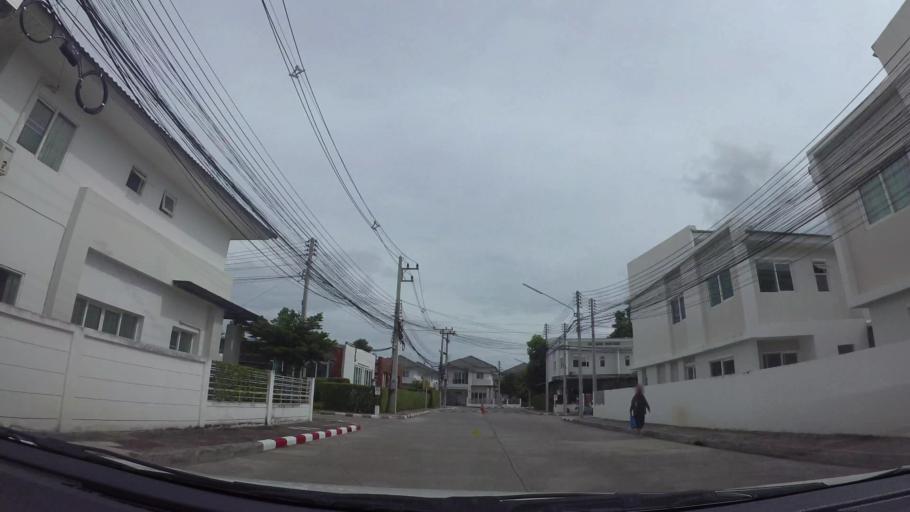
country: TH
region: Chiang Mai
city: Chiang Mai
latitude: 18.7475
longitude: 98.9665
